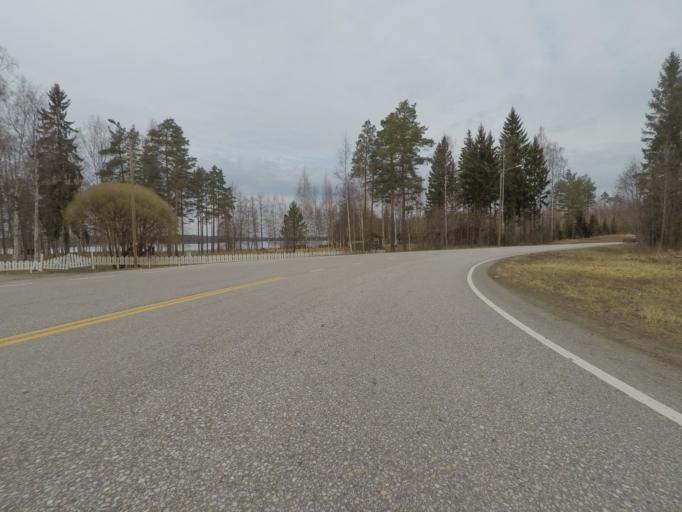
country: FI
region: Central Finland
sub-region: Joutsa
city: Joutsa
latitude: 61.7156
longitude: 26.0702
